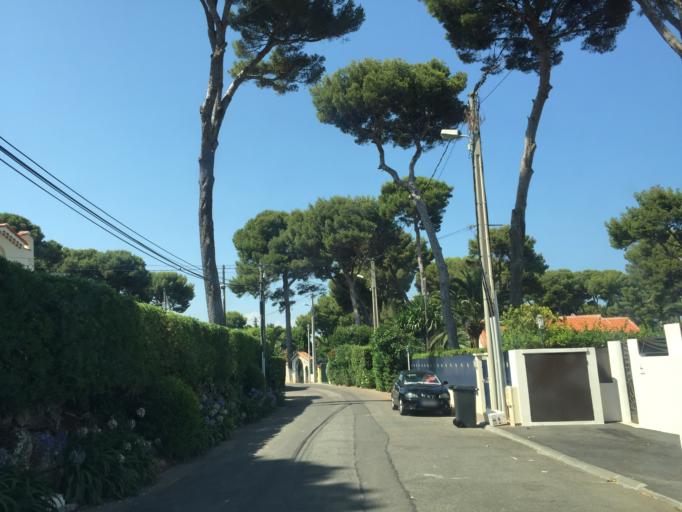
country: FR
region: Provence-Alpes-Cote d'Azur
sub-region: Departement des Alpes-Maritimes
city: Antibes
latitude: 43.5672
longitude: 7.1366
